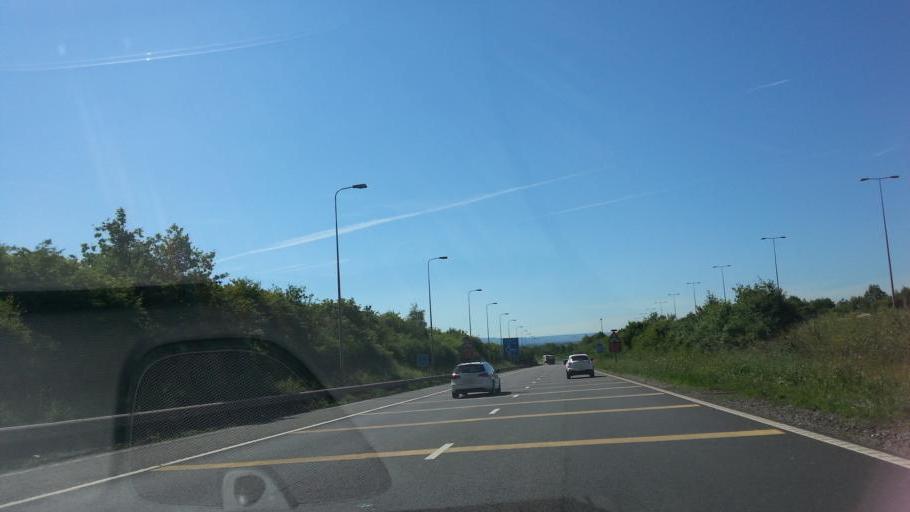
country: GB
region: England
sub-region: Worcestershire
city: Bredon
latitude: 52.0518
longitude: -2.1375
